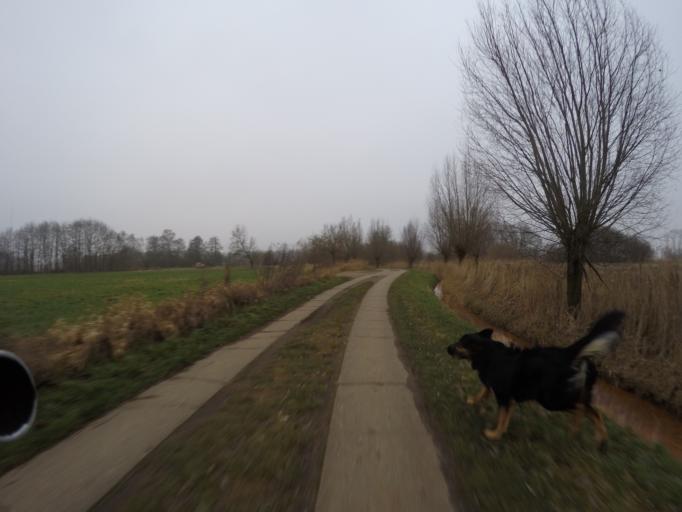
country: DE
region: Schleswig-Holstein
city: Borstel-Hohenraden
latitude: 53.6722
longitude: 9.8196
